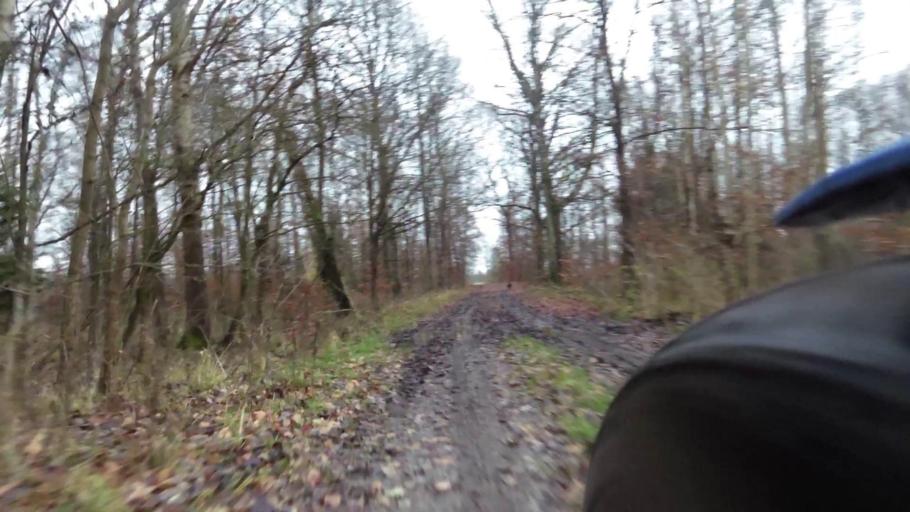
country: PL
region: West Pomeranian Voivodeship
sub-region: Powiat szczecinecki
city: Szczecinek
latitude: 53.6688
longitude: 16.6484
